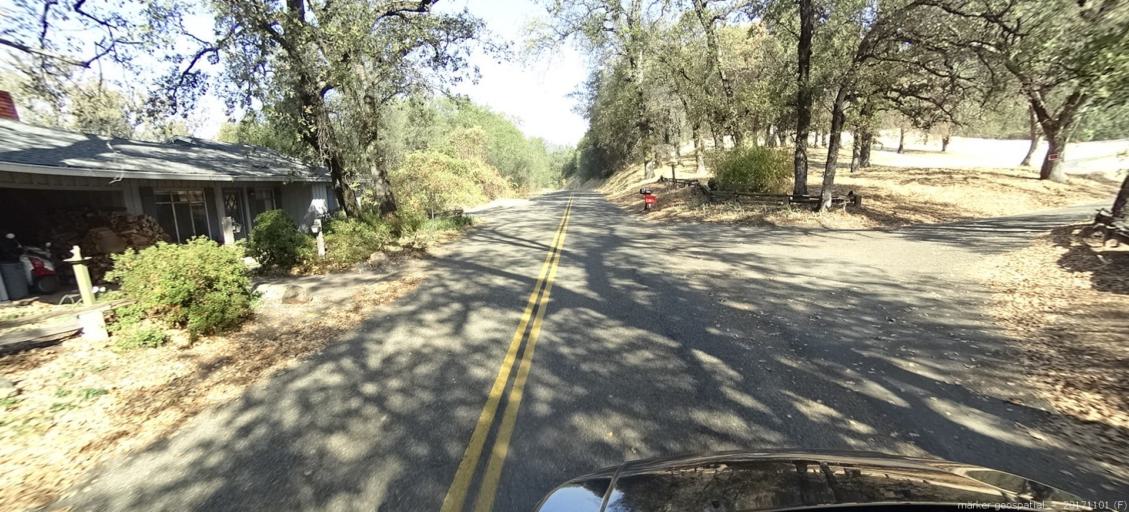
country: US
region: California
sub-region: Shasta County
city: Shasta Lake
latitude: 40.7137
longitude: -122.3286
